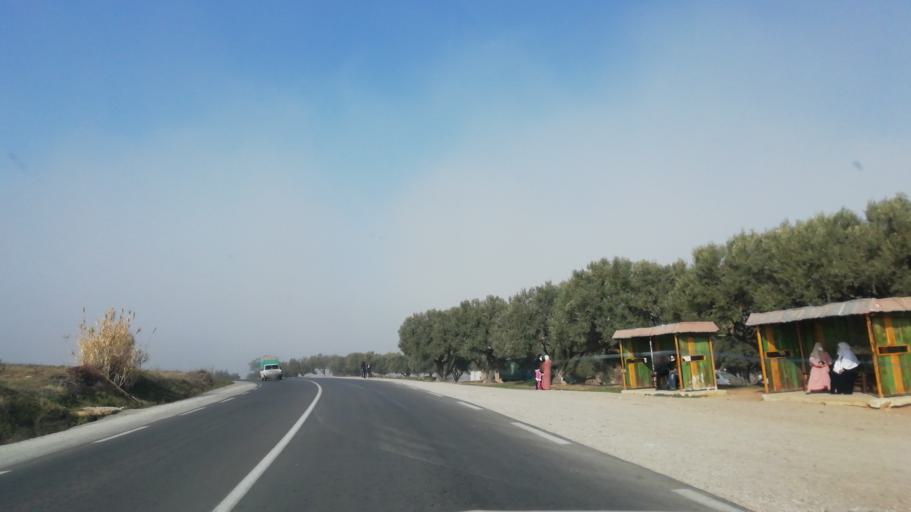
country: DZ
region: Mascara
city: Mascara
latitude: 35.5265
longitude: 0.3463
